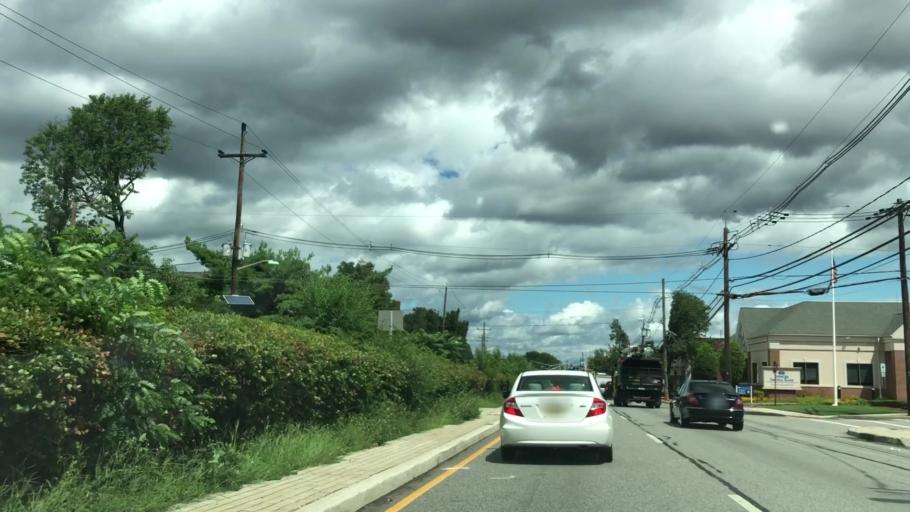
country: US
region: New Jersey
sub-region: Passaic County
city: Clifton
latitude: 40.8786
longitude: -74.1549
